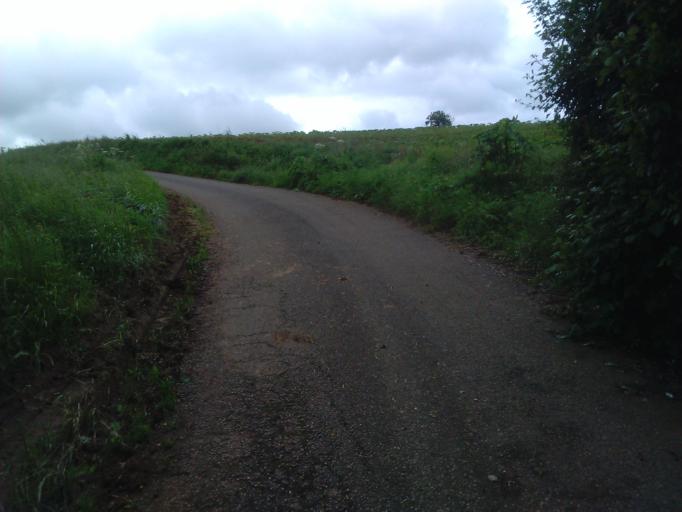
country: FR
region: Centre
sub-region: Departement du Cher
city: Sancerre
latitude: 47.3125
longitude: 2.7314
